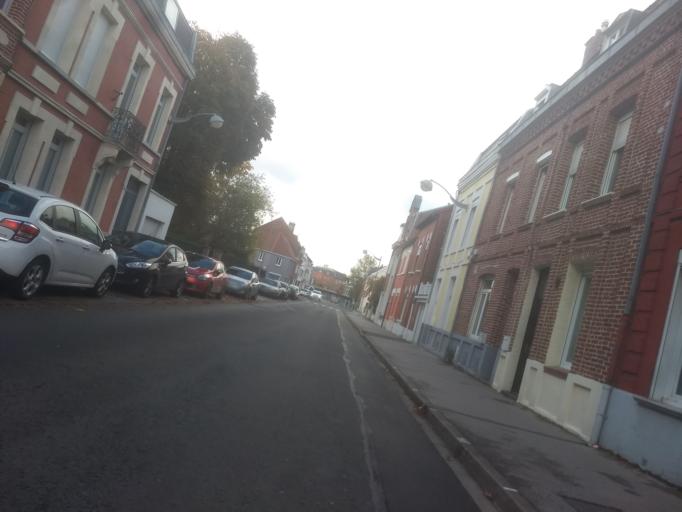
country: FR
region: Nord-Pas-de-Calais
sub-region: Departement du Pas-de-Calais
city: Arras
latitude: 50.2853
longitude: 2.7835
